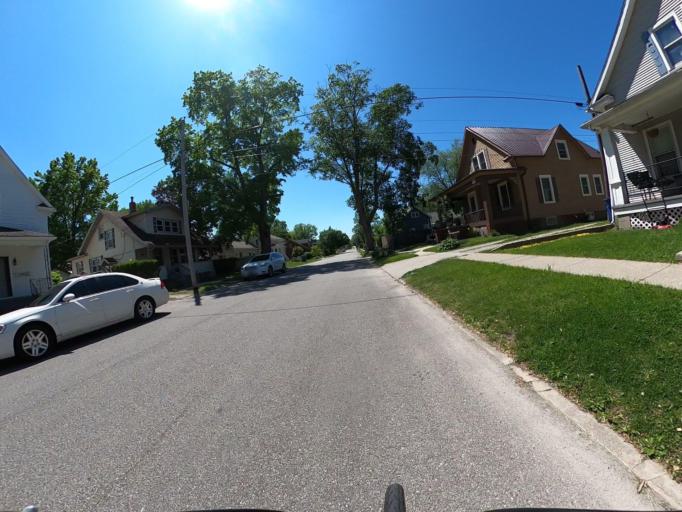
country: US
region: Indiana
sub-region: LaPorte County
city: LaPorte
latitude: 41.6057
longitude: -86.7307
